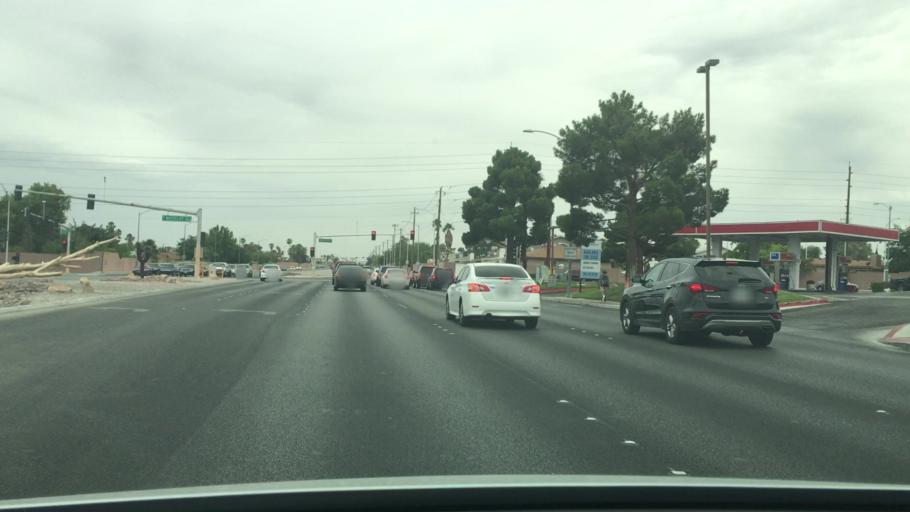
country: US
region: Nevada
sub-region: Clark County
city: Spring Valley
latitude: 36.1749
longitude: -115.2599
